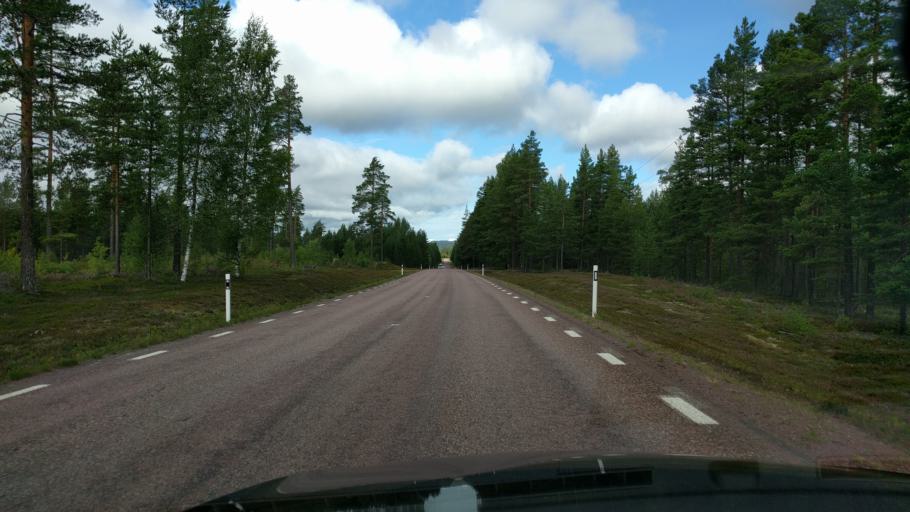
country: SE
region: Dalarna
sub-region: Mora Kommun
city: Mora
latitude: 61.0705
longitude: 14.3782
